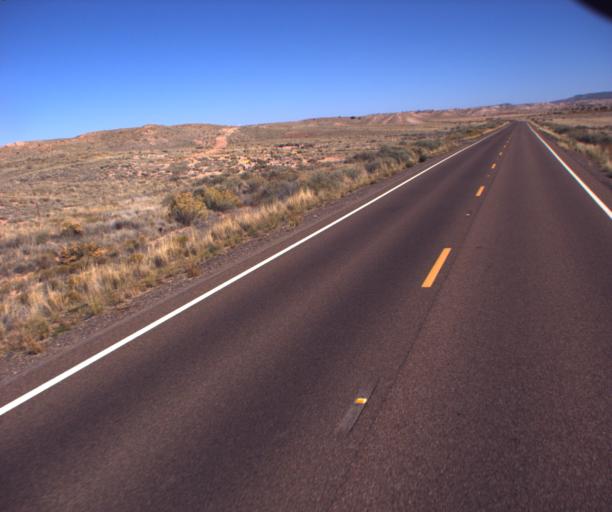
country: US
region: Arizona
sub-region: Navajo County
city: Joseph City
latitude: 35.1670
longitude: -110.4507
